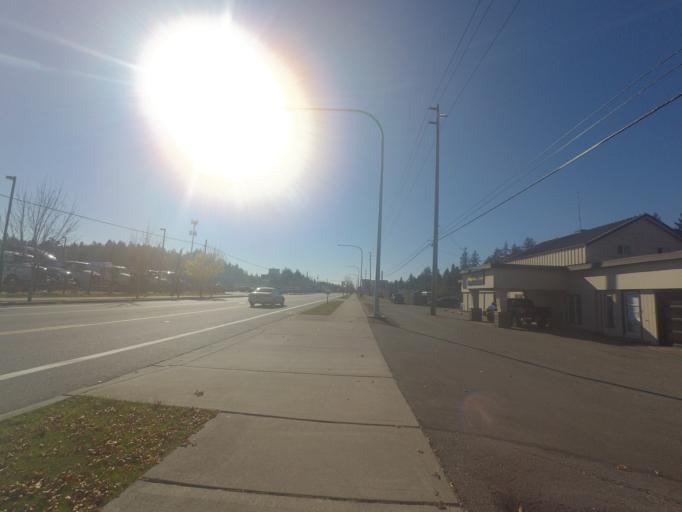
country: US
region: Washington
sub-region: Pierce County
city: McChord Air Force Base
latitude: 47.1444
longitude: -122.5129
